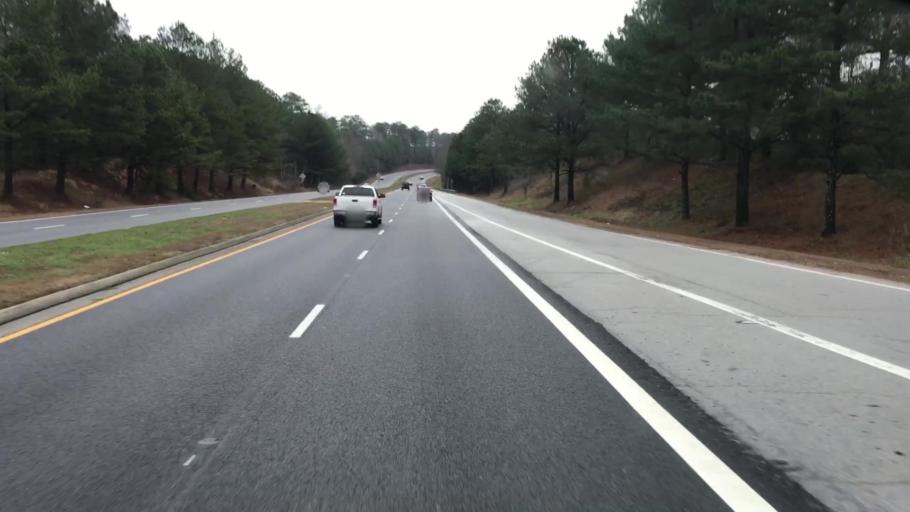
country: US
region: Georgia
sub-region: Gwinnett County
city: Snellville
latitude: 33.8896
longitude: -84.0517
